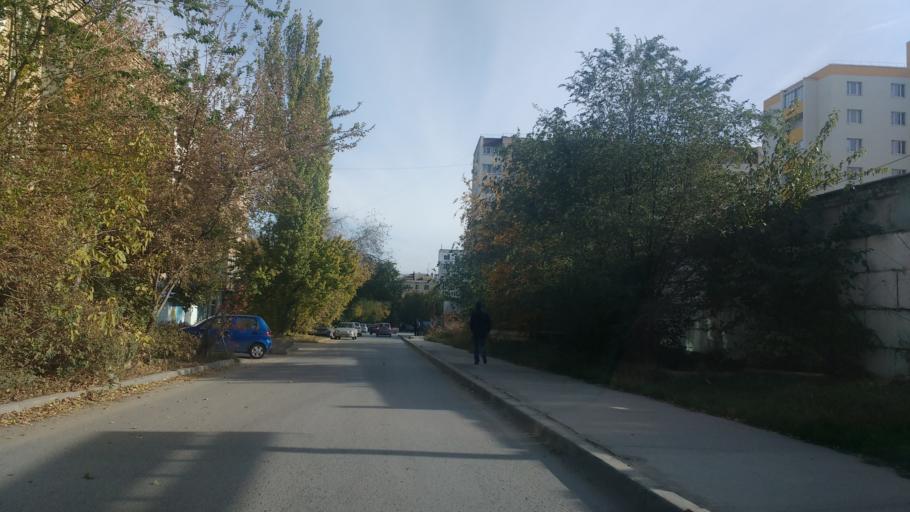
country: RU
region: Volgograd
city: Krasnoslobodsk
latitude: 48.7636
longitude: 44.5522
